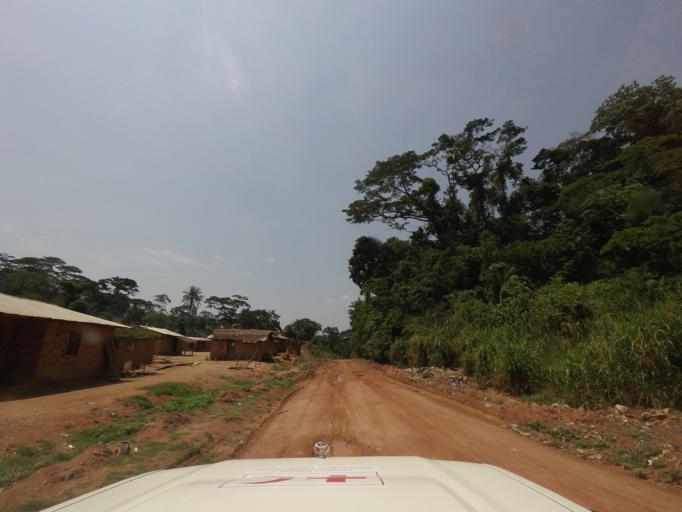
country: LR
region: Lofa
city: Voinjama
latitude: 8.3850
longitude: -9.7596
